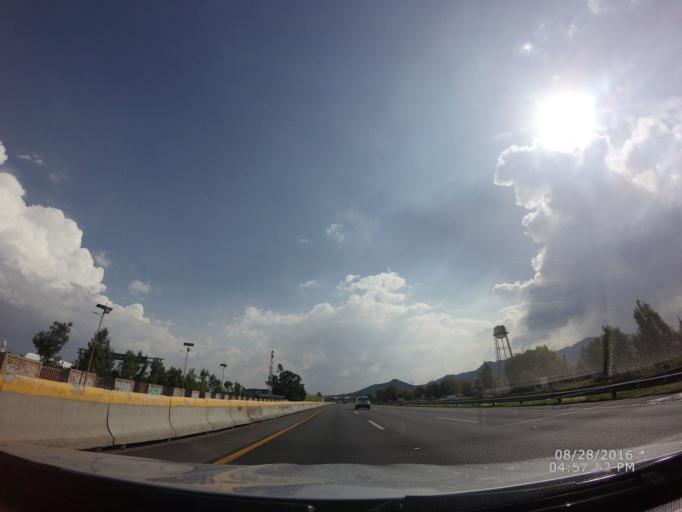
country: MX
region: Mexico
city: Ecatepec
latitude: 19.6131
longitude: -99.0327
